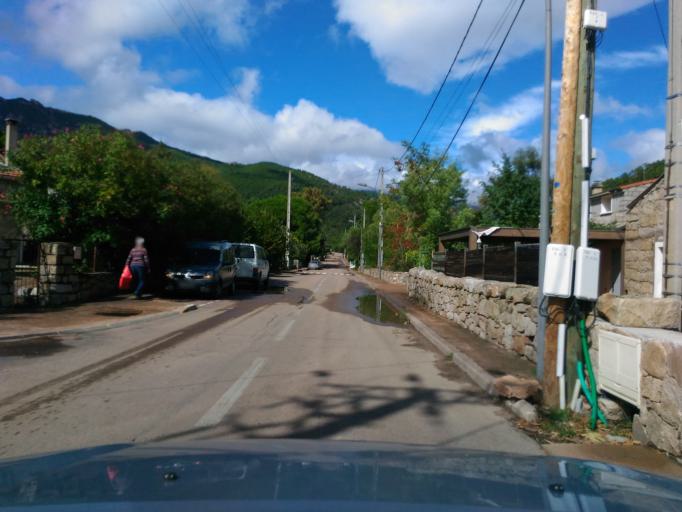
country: FR
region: Corsica
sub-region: Departement de la Corse-du-Sud
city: Porto-Vecchio
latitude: 41.7094
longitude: 9.3122
